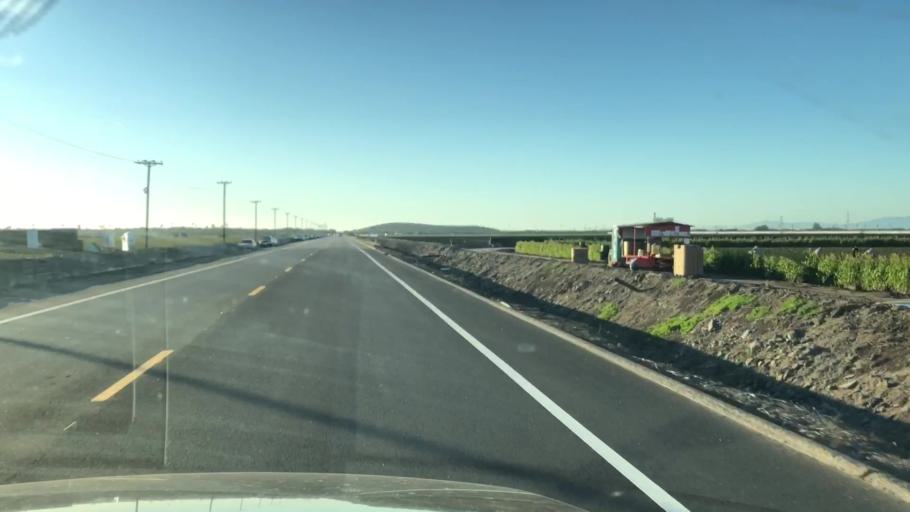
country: US
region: California
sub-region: Ventura County
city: Oxnard Shores
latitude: 34.1978
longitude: -119.2244
